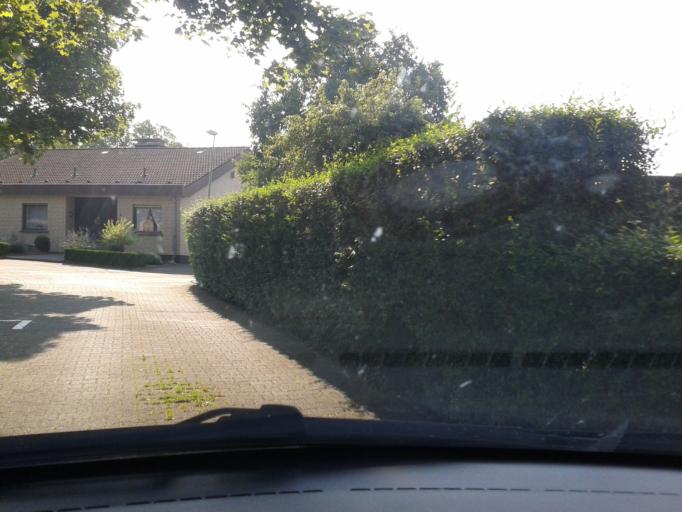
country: DE
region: North Rhine-Westphalia
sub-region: Regierungsbezirk Detmold
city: Paderborn
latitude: 51.7051
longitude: 8.7805
